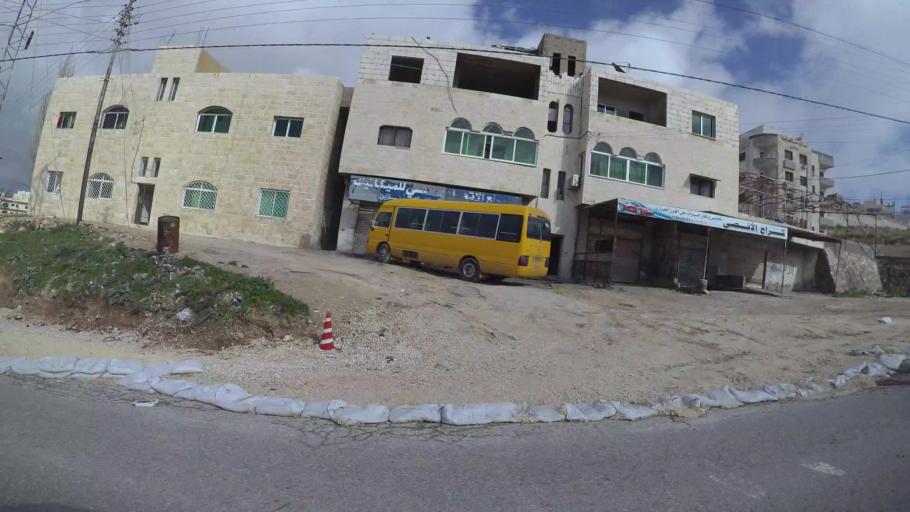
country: JO
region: Amman
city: Al Jubayhah
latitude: 32.0627
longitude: 35.8685
